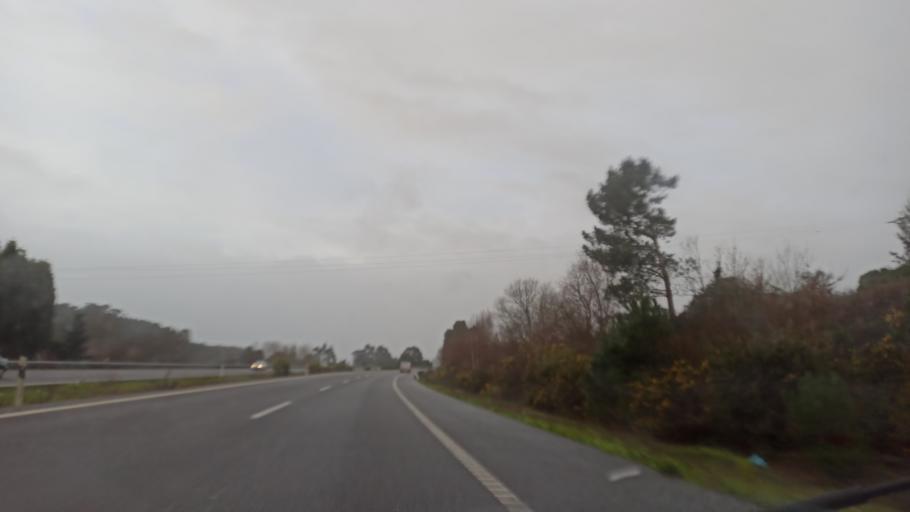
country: ES
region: Galicia
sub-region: Provincia da Coruna
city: Abegondo
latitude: 43.2556
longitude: -8.2646
